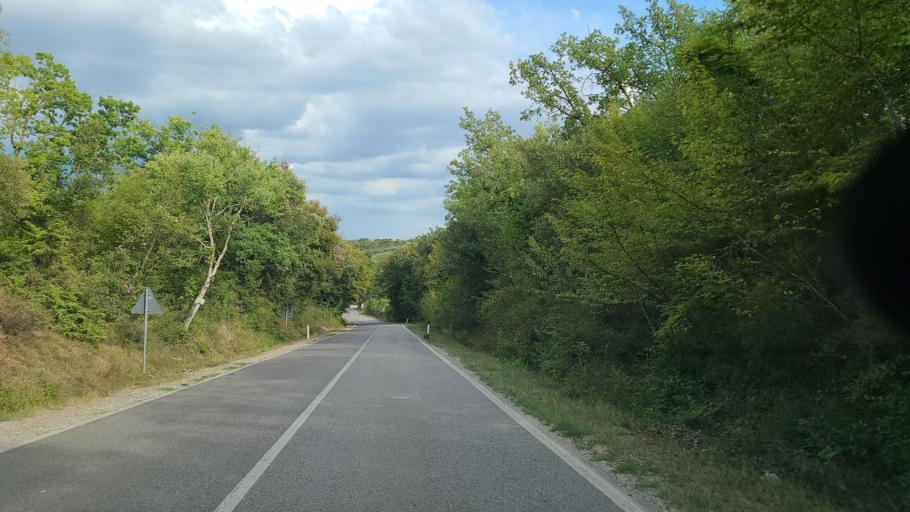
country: IT
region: Tuscany
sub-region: Provincia di Siena
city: San Gimignano
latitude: 43.4876
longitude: 10.9891
